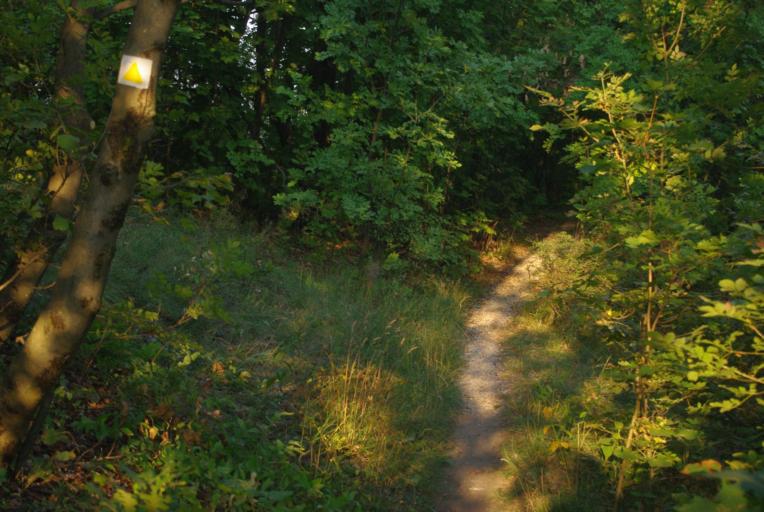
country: HU
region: Pest
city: Solymar
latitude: 47.5760
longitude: 18.9667
